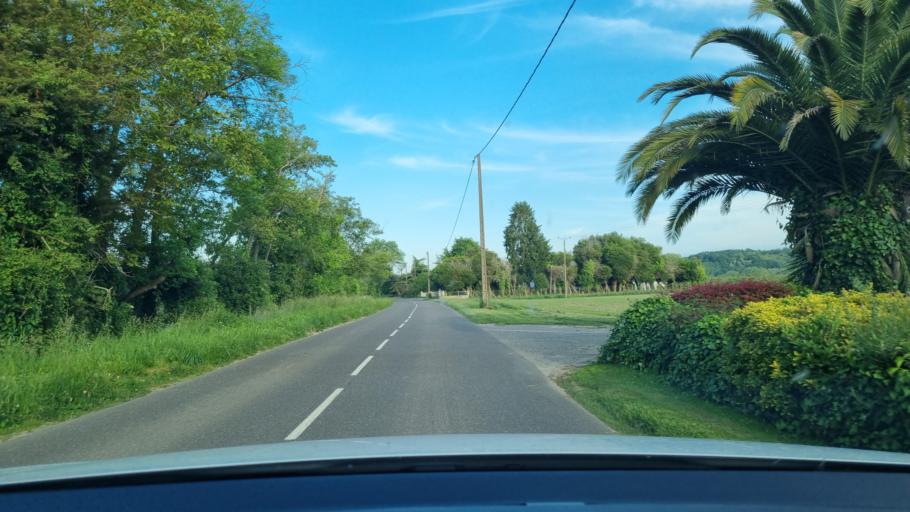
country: FR
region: Aquitaine
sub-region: Departement des Landes
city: Peyrehorade
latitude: 43.5403
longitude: -1.1257
